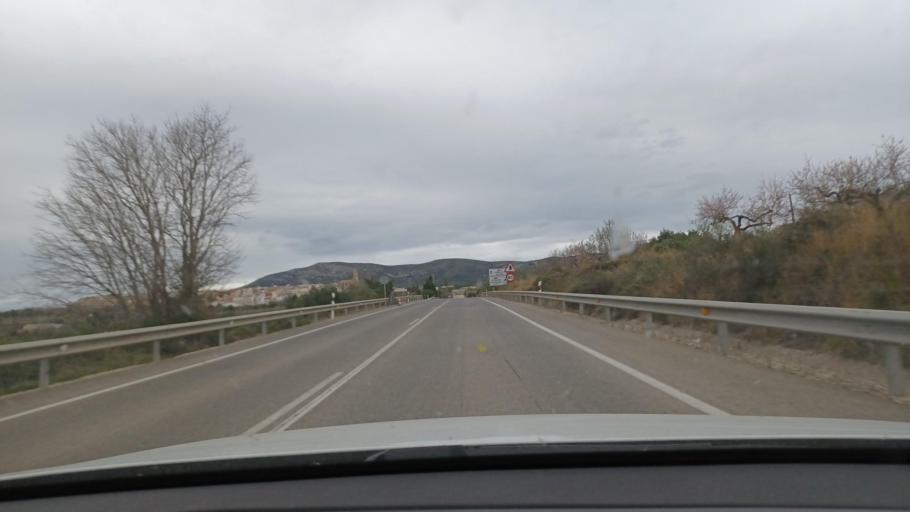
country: ES
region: Valencia
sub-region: Provincia de Castello
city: Traiguera
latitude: 40.5229
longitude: 0.3039
